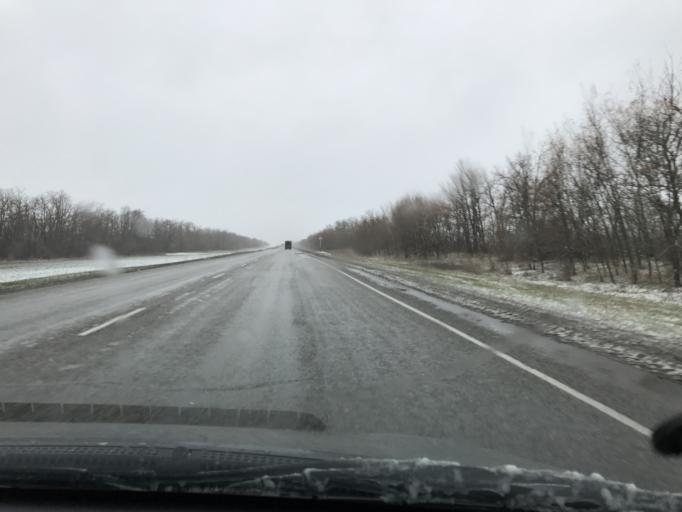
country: RU
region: Rostov
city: Mechetinskaya
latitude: 46.7379
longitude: 40.4726
